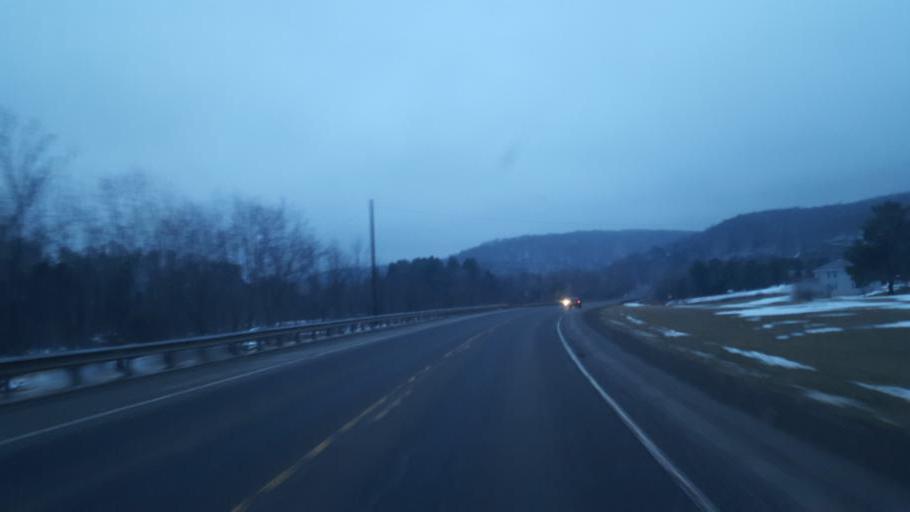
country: US
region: Pennsylvania
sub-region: Potter County
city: Coudersport
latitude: 41.7685
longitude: -78.1264
